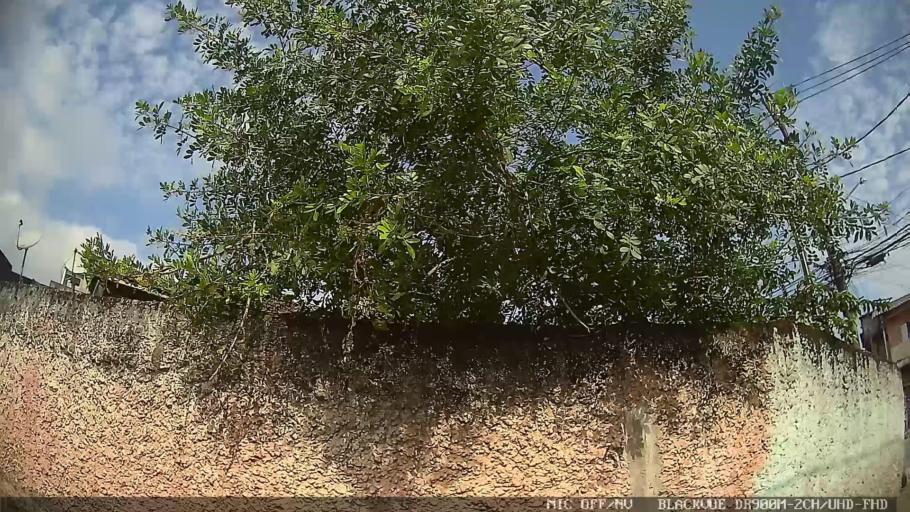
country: BR
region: Sao Paulo
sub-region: Santos
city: Santos
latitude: -23.9502
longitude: -46.3018
